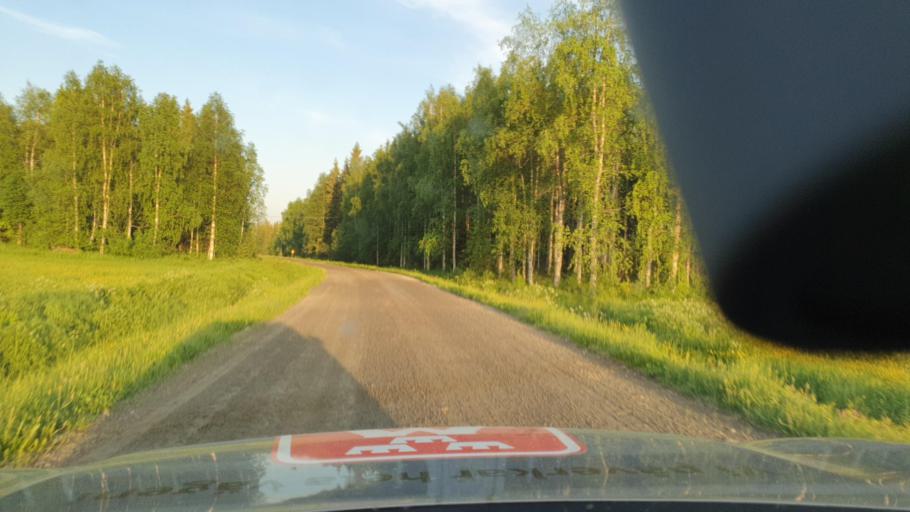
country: SE
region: Norrbotten
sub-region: Bodens Kommun
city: Boden
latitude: 66.1033
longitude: 21.5804
